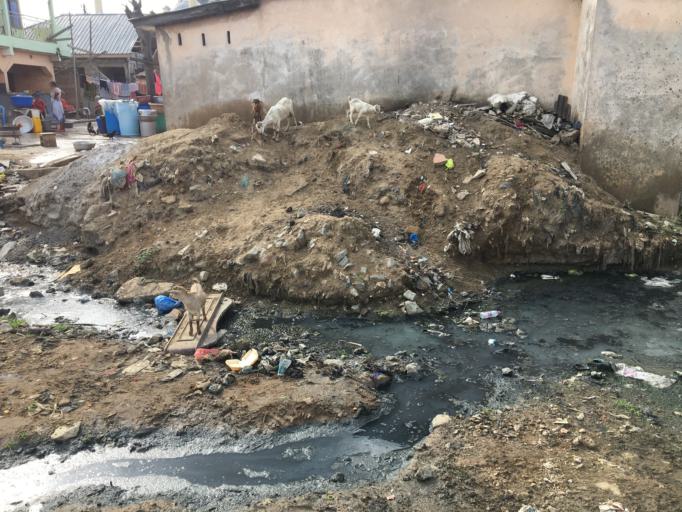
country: GH
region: Greater Accra
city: Accra
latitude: 5.5914
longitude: -0.1912
